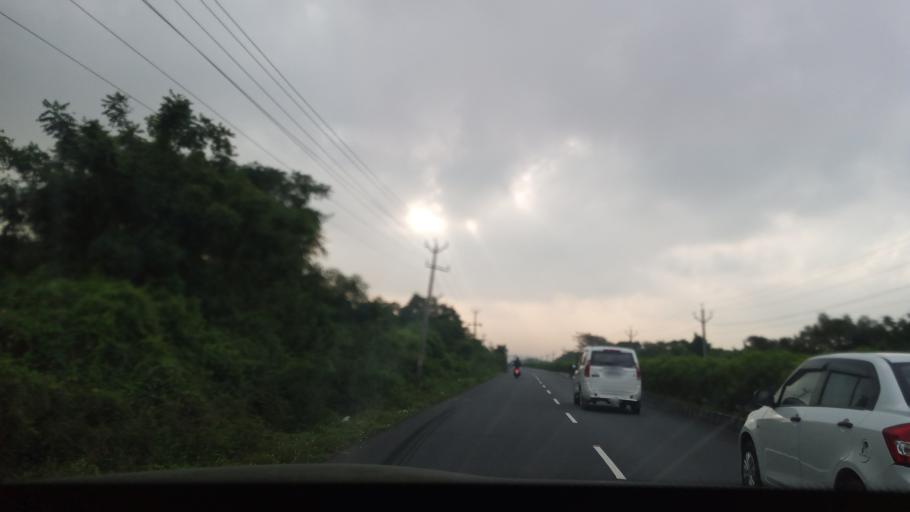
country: IN
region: Tamil Nadu
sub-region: Kancheepuram
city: Vengavasal
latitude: 12.8142
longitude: 80.1799
